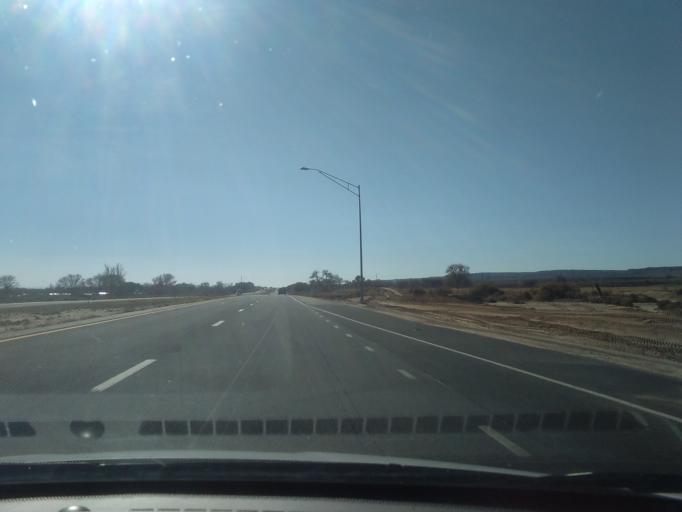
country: US
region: New Mexico
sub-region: Valencia County
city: Jarales
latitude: 34.6254
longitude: -106.7834
